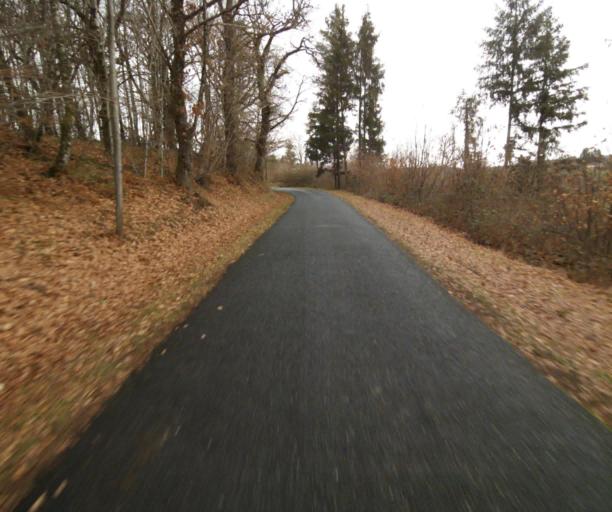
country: FR
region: Limousin
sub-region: Departement de la Correze
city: Saint-Mexant
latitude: 45.3043
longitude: 1.6413
